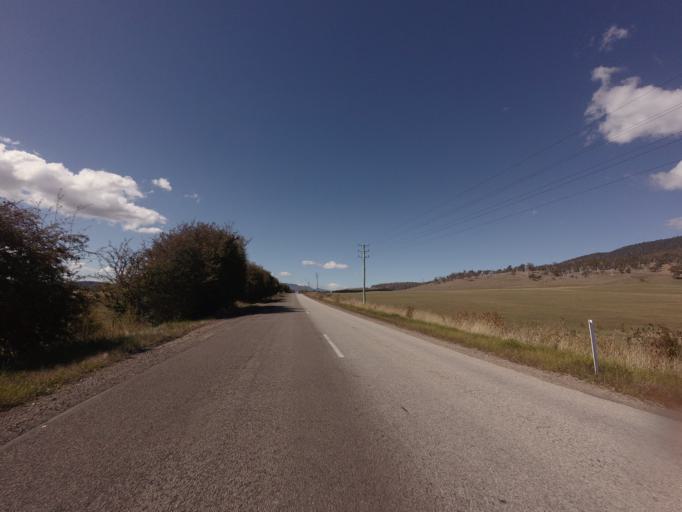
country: AU
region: Tasmania
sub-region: Break O'Day
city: St Helens
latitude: -41.6260
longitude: 147.9932
